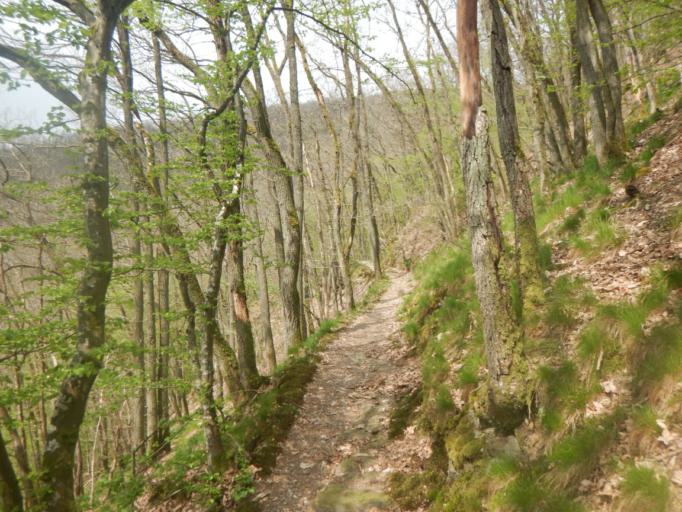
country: LU
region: Diekirch
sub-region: Canton de Wiltz
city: Esch-sur-Sure
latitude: 49.9128
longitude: 5.9383
